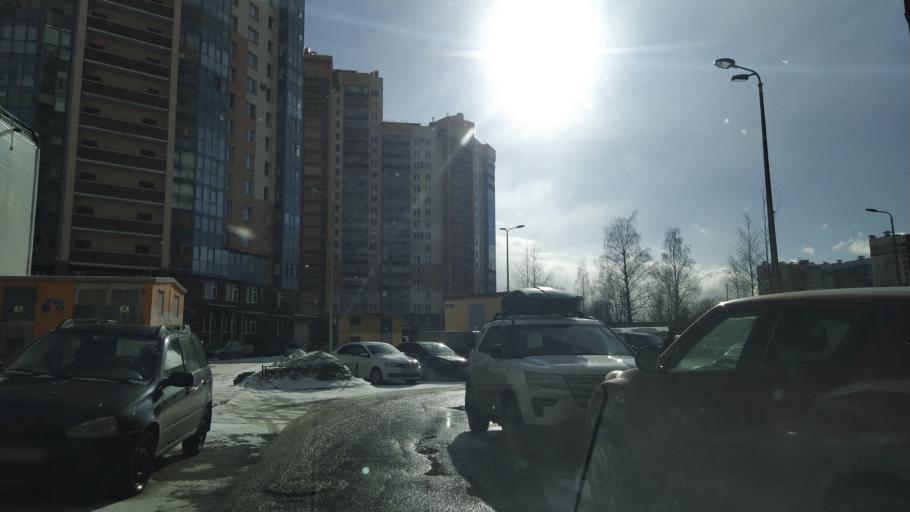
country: RU
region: Leningrad
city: Akademicheskoe
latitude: 60.0146
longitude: 30.3871
